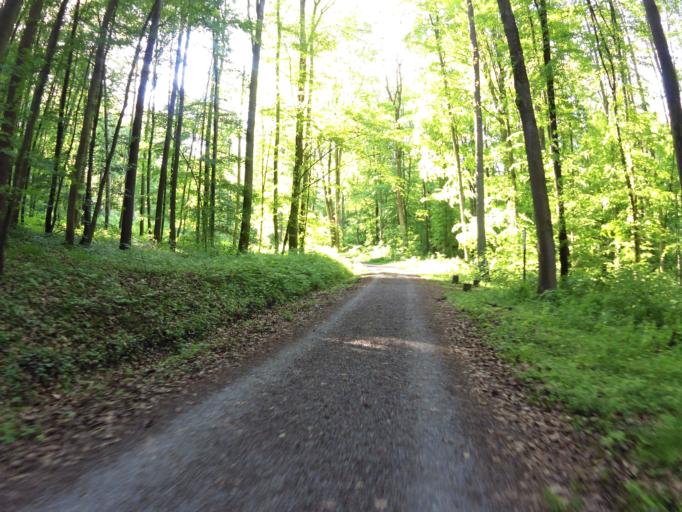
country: DE
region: Bavaria
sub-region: Regierungsbezirk Unterfranken
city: Reichenberg
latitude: 49.7489
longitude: 9.9141
